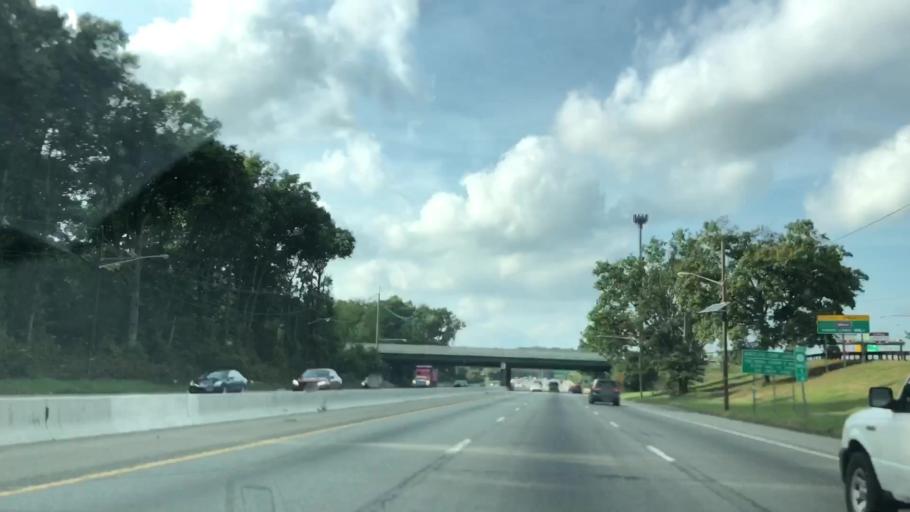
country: US
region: New Jersey
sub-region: Passaic County
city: Clifton
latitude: 40.8511
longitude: -74.1740
